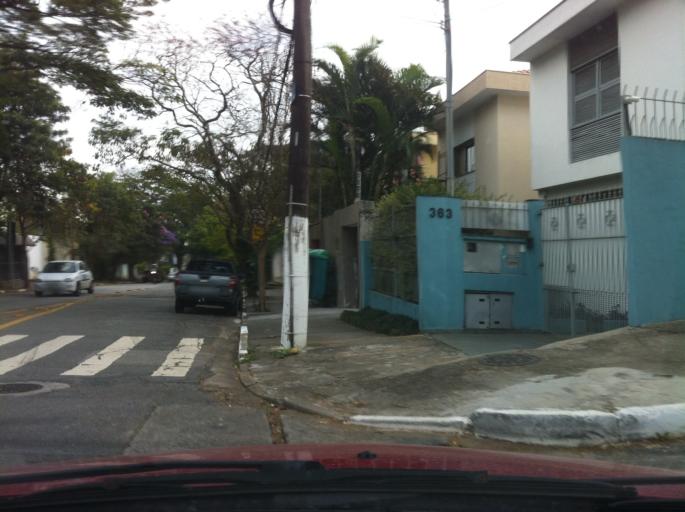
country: BR
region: Sao Paulo
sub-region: Diadema
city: Diadema
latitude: -23.6401
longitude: -46.6940
